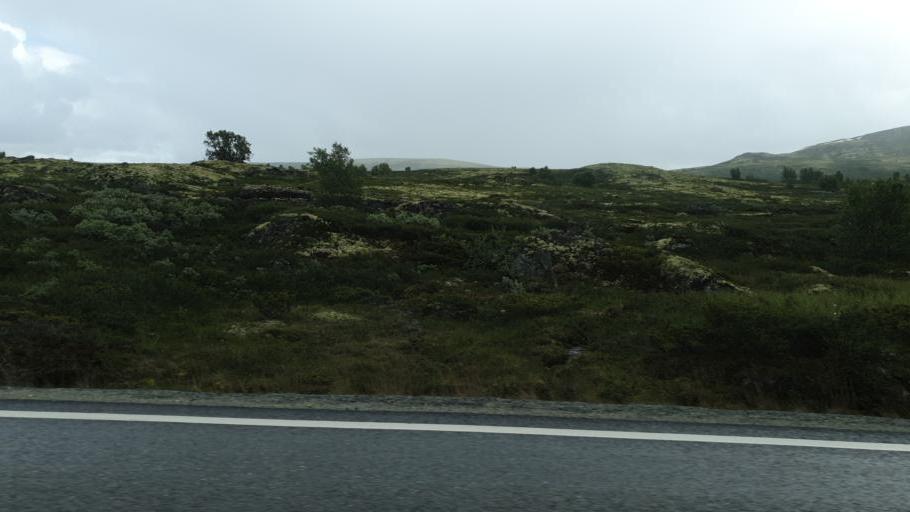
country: NO
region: Sor-Trondelag
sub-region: Oppdal
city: Oppdal
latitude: 62.2667
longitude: 9.5789
